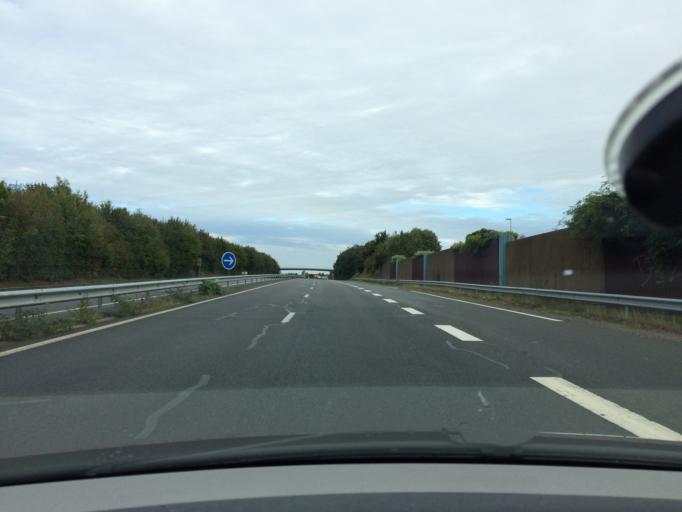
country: FR
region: Brittany
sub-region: Departement d'Ille-et-Vilaine
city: Vern-sur-Seiche
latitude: 48.0369
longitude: -1.6017
